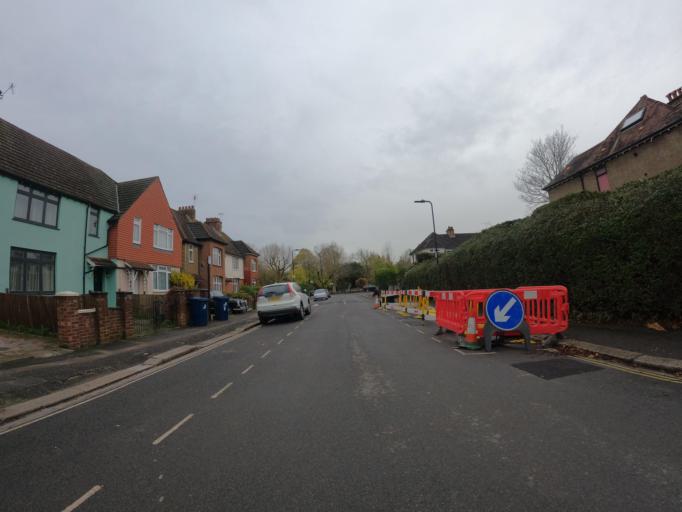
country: GB
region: England
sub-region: Greater London
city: Ealing
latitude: 51.4997
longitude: -0.3018
